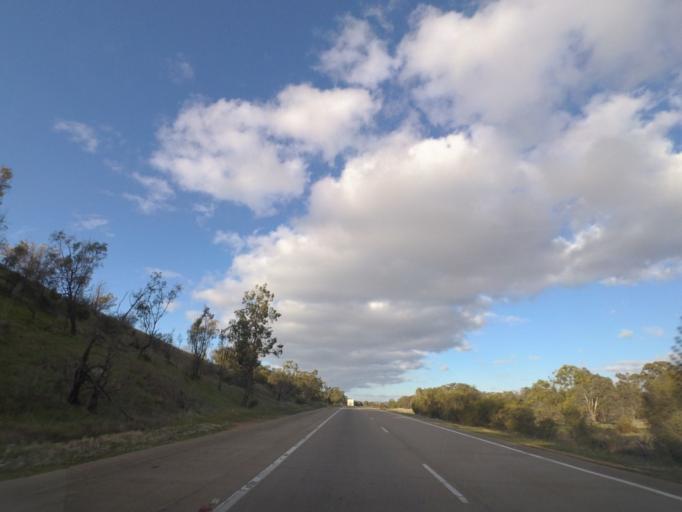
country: AU
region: New South Wales
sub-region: Yass Valley
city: Yass
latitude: -34.8019
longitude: 148.4948
